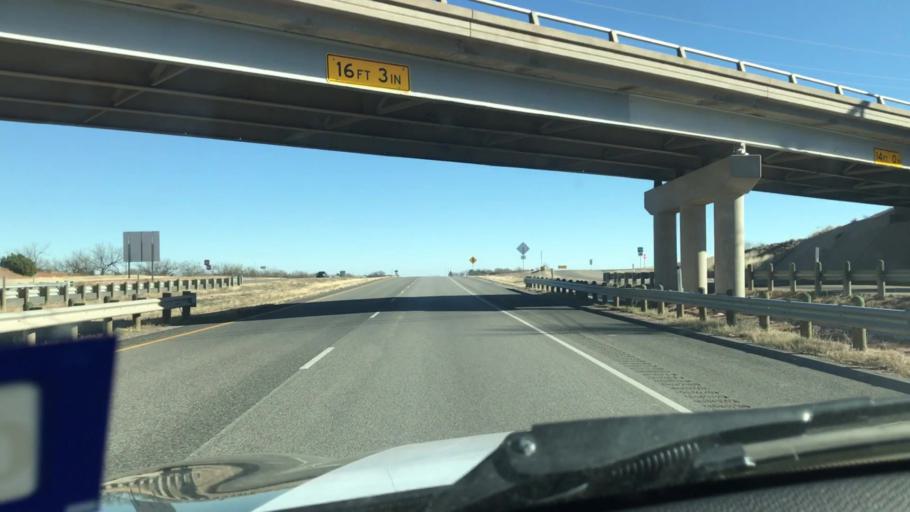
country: US
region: Texas
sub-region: Scurry County
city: Snyder
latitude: 32.7312
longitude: -100.9018
